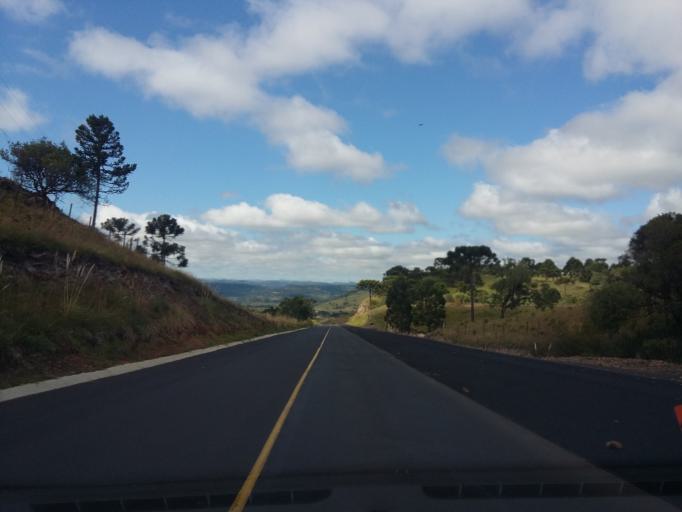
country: BR
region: Santa Catarina
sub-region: Sao Joaquim
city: Sao Joaquim
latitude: -28.0569
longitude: -50.0739
